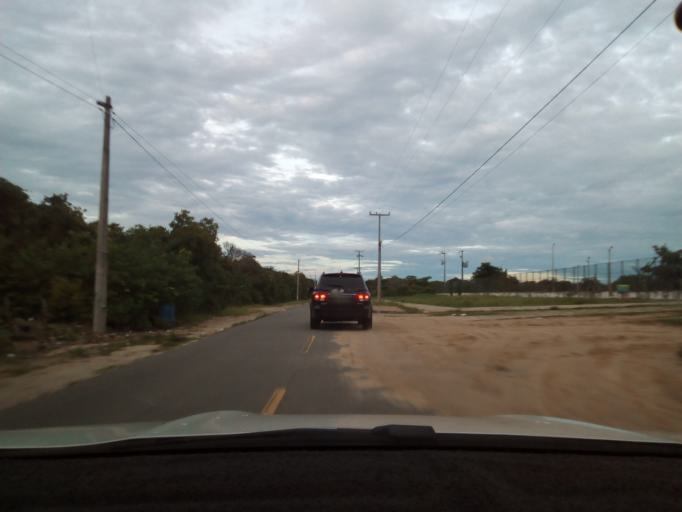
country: BR
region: Ceara
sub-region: Beberibe
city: Beberibe
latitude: -4.1860
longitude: -38.1150
